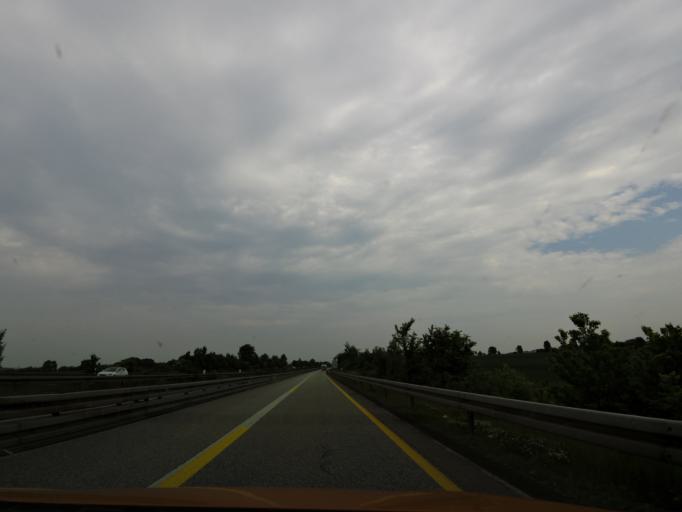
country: DE
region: Mecklenburg-Vorpommern
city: Wismar
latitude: 53.8616
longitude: 11.3949
